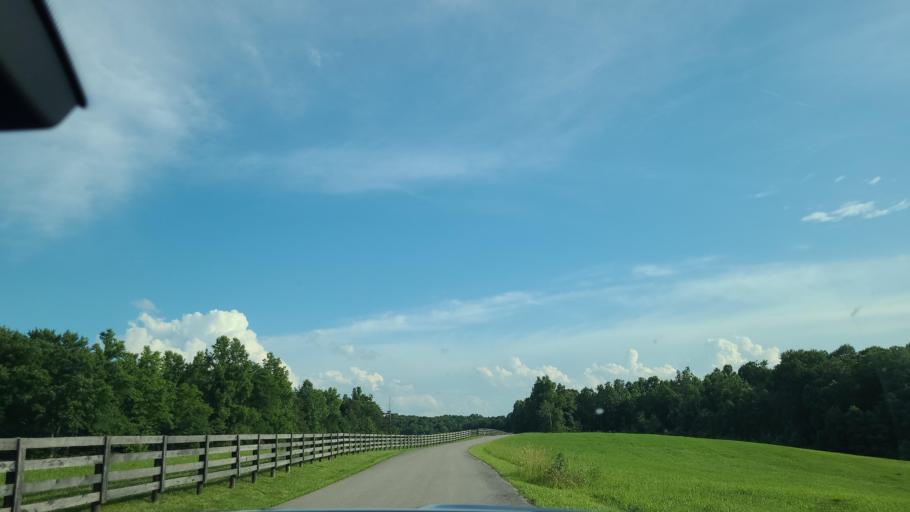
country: US
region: Kentucky
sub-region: Whitley County
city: Corbin
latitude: 36.8913
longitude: -84.2335
